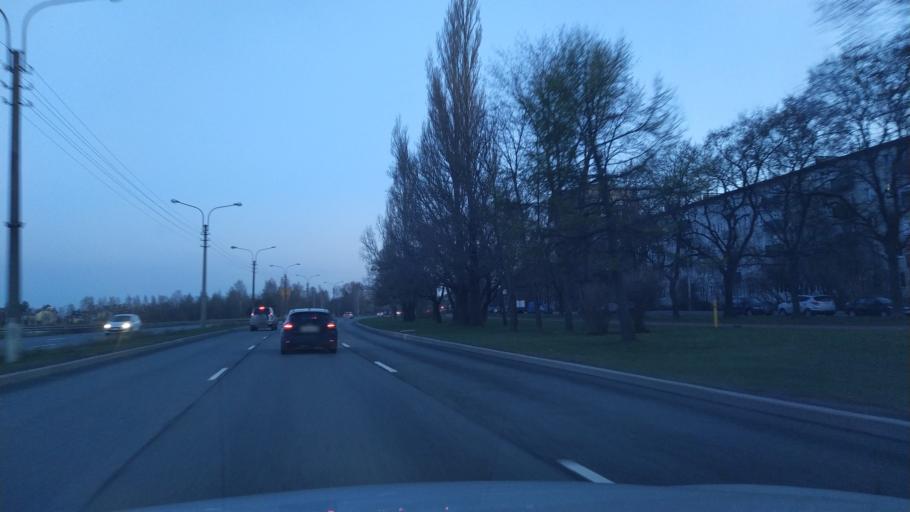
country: RU
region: St.-Petersburg
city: Sestroretsk
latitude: 60.0977
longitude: 29.9801
